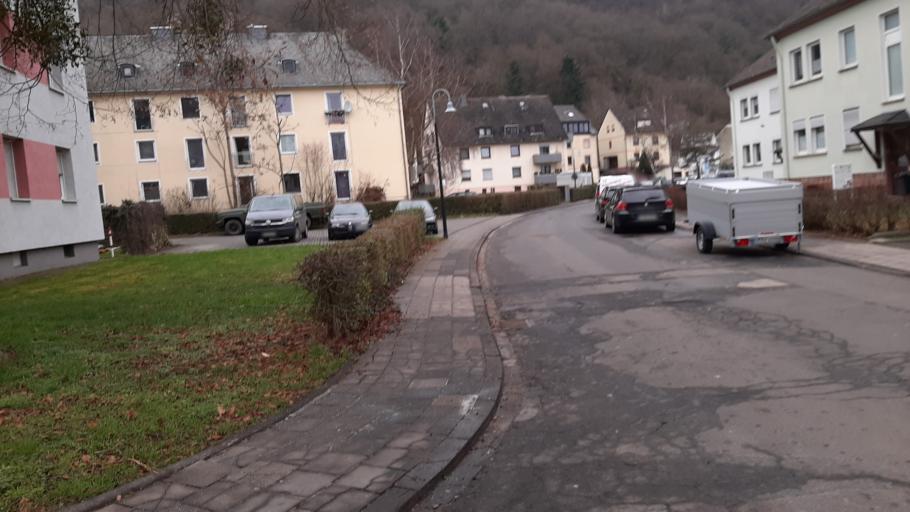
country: DE
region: Rheinland-Pfalz
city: Trier
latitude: 49.7430
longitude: 6.6104
